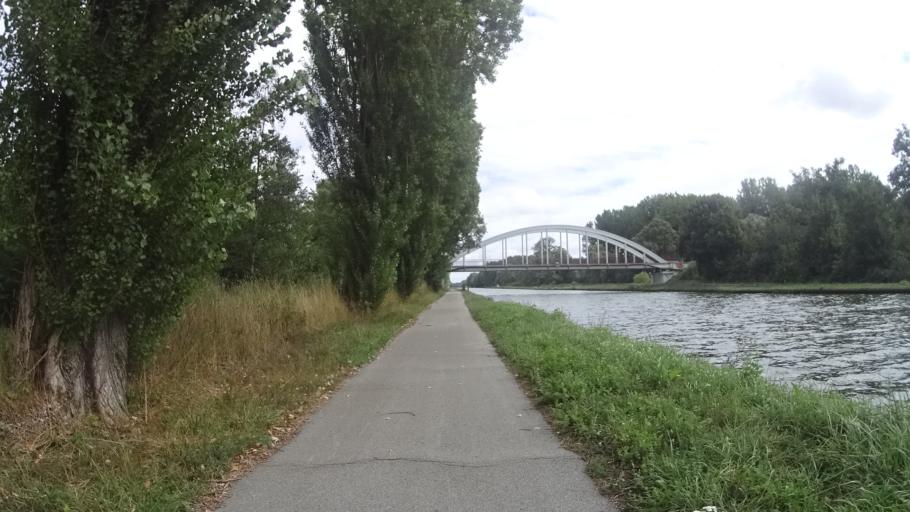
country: FR
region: Picardie
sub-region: Departement de l'Aisne
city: Blerancourt
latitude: 49.5784
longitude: 3.1193
